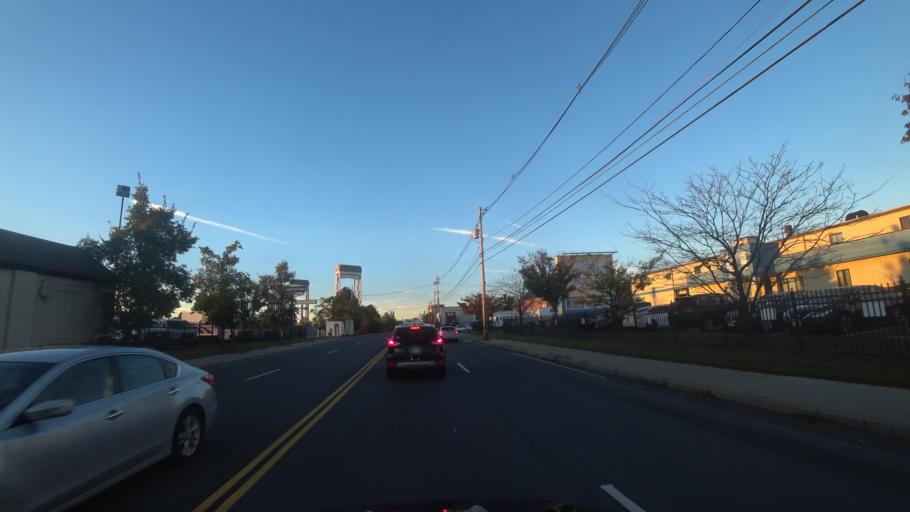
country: US
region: Massachusetts
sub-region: Suffolk County
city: Chelsea
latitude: 42.3908
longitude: -71.0227
